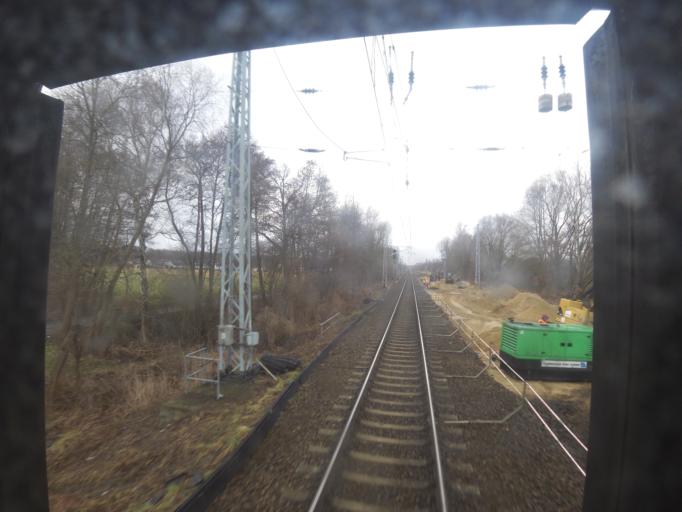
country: DE
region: Brandenburg
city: Rangsdorf
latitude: 52.2895
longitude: 13.4325
